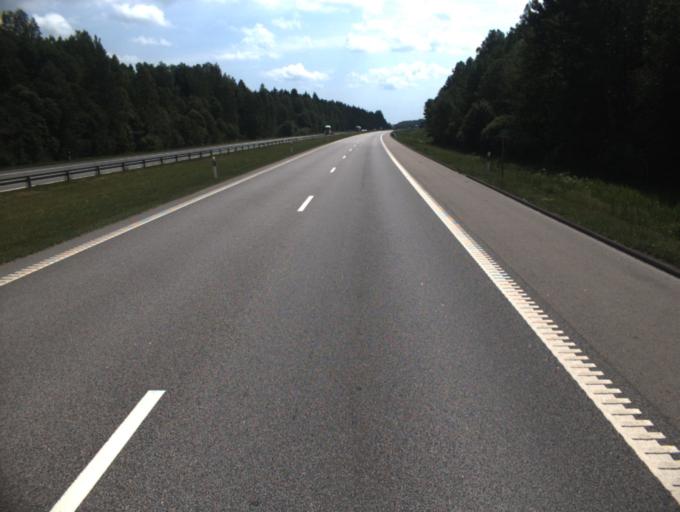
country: LT
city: Rietavas
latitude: 55.6928
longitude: 21.6717
